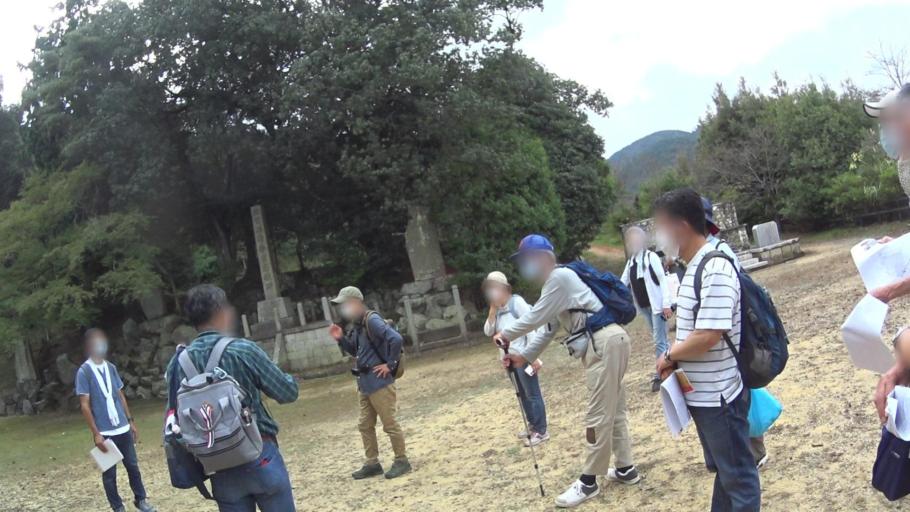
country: JP
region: Osaka
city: Kishiwada
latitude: 34.5038
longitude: 135.3364
